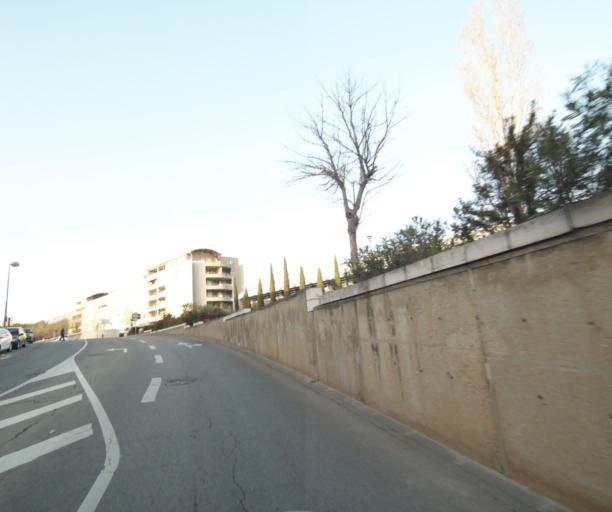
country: FR
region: Provence-Alpes-Cote d'Azur
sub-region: Departement des Bouches-du-Rhone
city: Saint-Victoret
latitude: 43.4257
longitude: 5.2723
